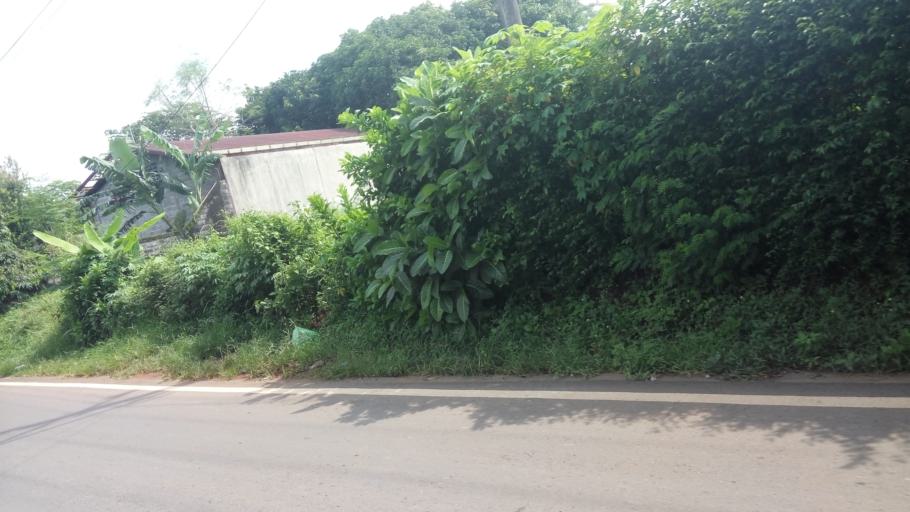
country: ID
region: Central Java
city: Ungaran
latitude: -7.0711
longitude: 110.4404
